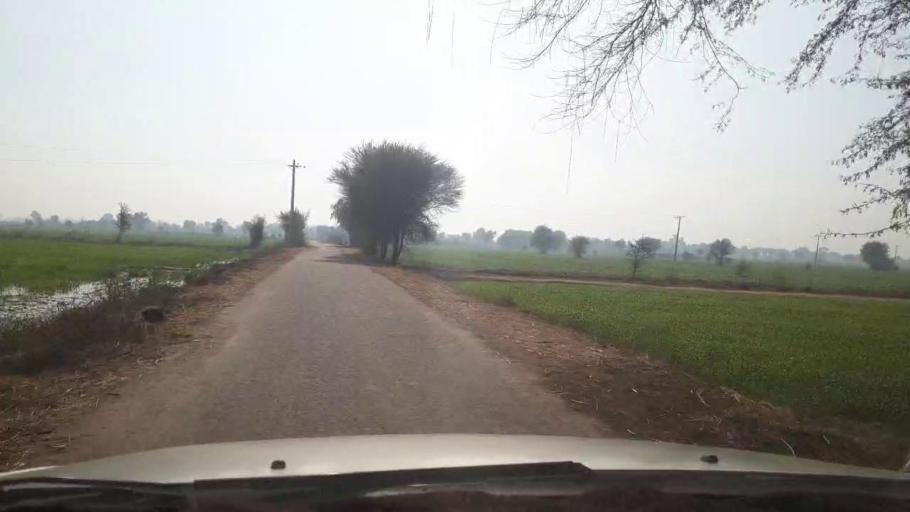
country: PK
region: Sindh
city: Khanpur
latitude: 27.7419
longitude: 69.5049
